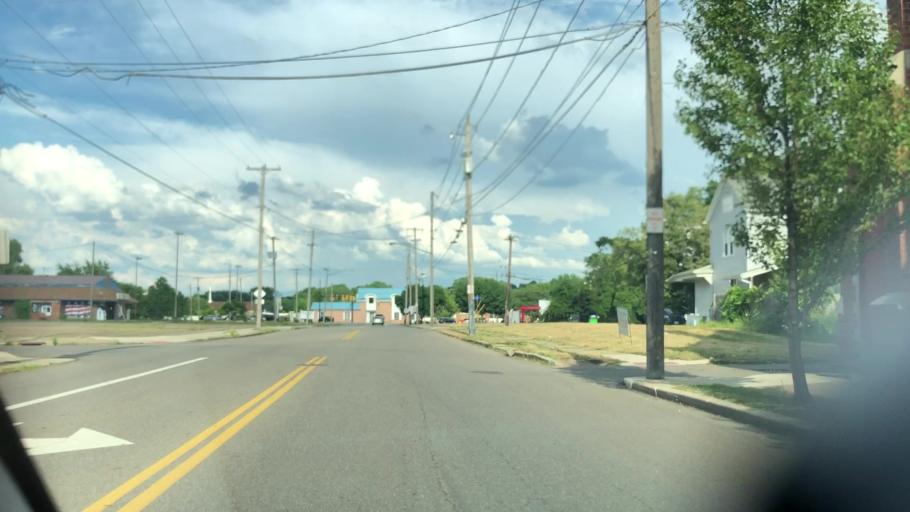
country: US
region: Ohio
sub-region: Summit County
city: Barberton
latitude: 41.0176
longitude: -81.6071
